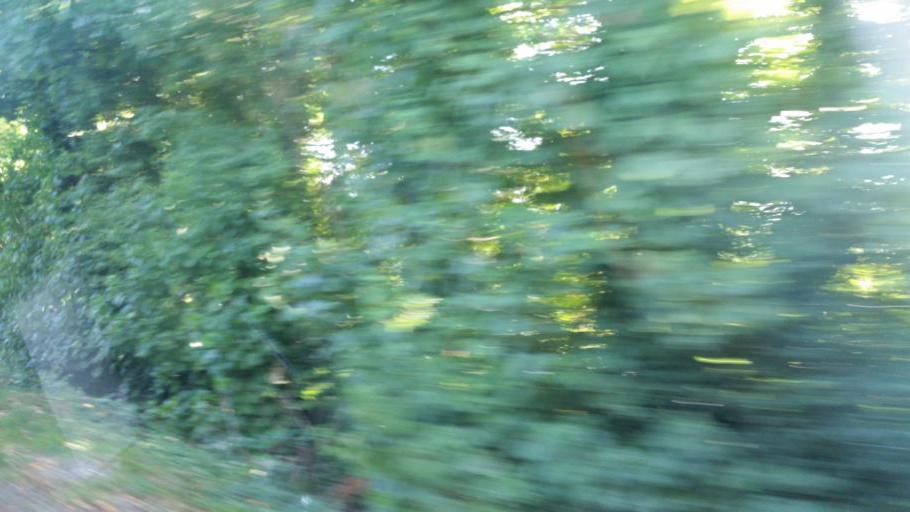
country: IE
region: Leinster
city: Hartstown
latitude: 53.4371
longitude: -6.4297
